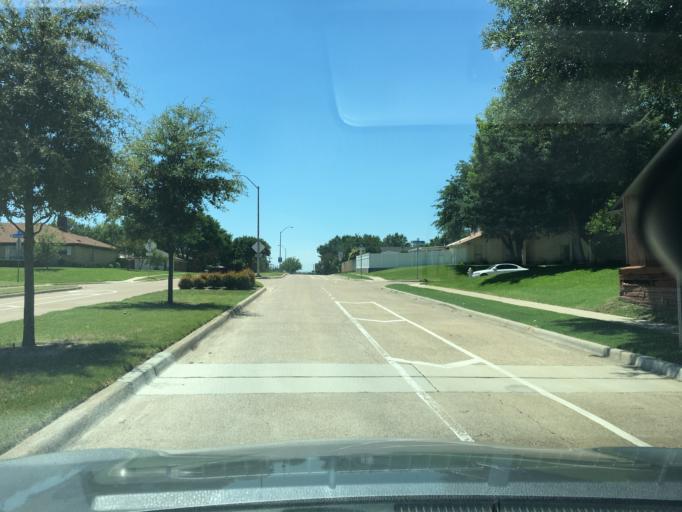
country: US
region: Texas
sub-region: Dallas County
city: Richardson
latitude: 32.9680
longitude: -96.6956
